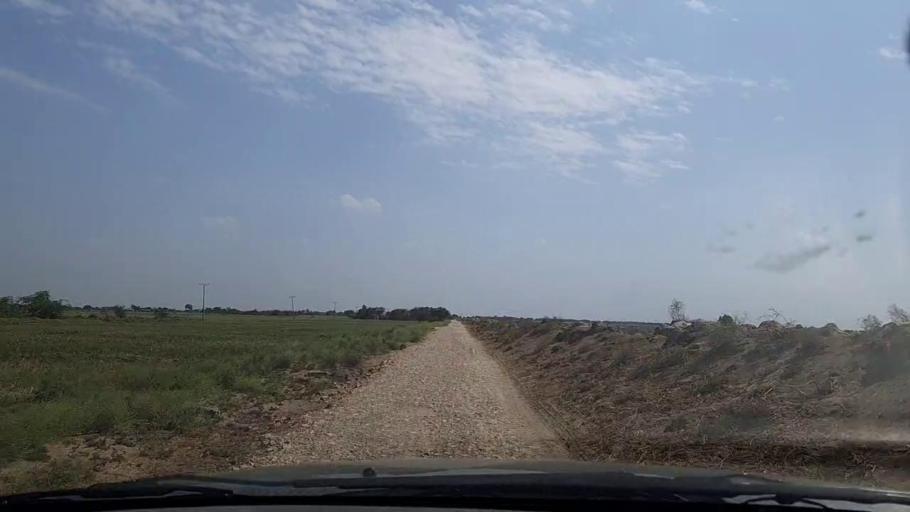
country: PK
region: Sindh
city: Mirpur Batoro
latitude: 24.5781
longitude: 68.1960
